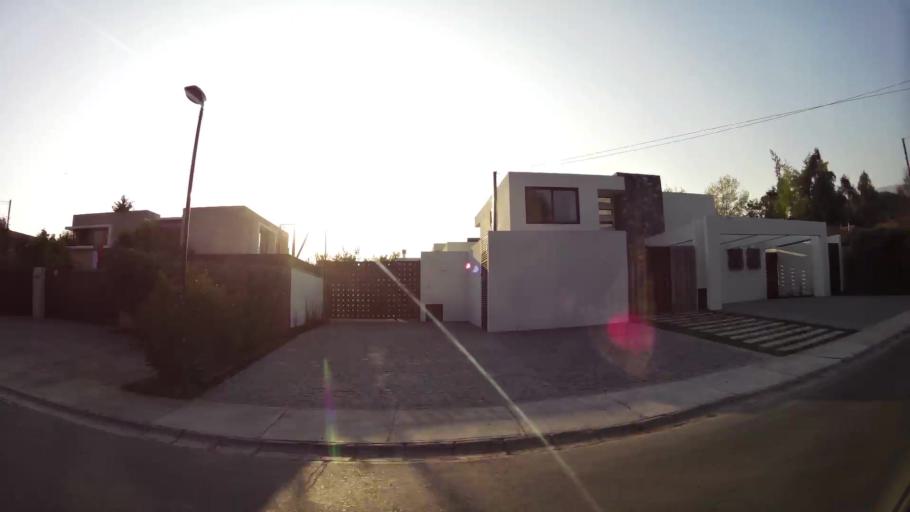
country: CL
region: Santiago Metropolitan
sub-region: Provincia de Santiago
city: Villa Presidente Frei, Nunoa, Santiago, Chile
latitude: -33.3382
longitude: -70.5109
